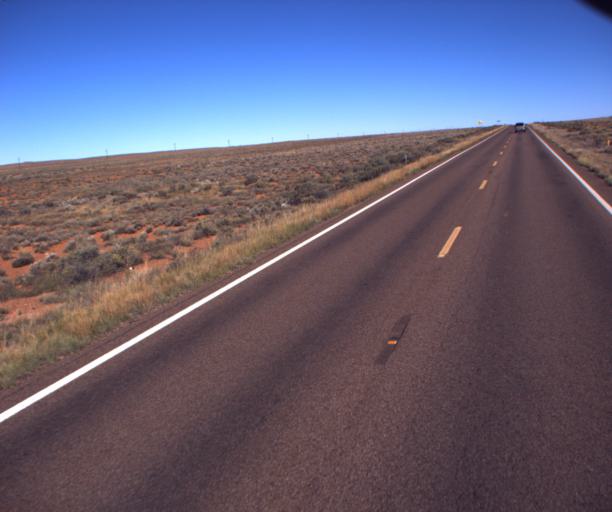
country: US
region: Arizona
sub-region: Navajo County
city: Holbrook
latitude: 34.7797
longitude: -110.1298
